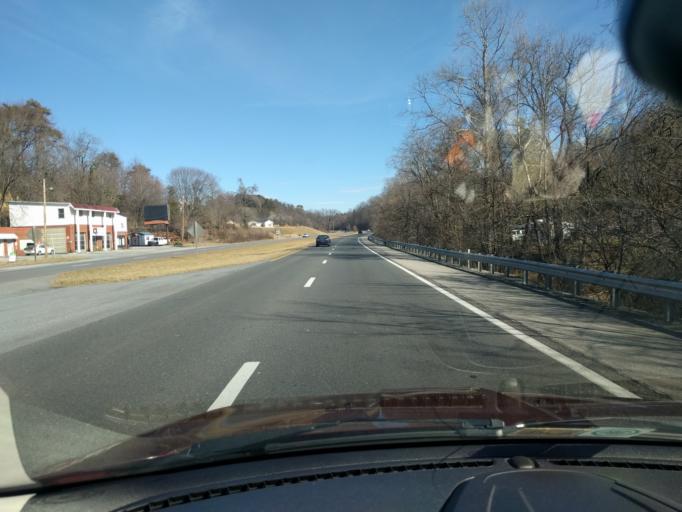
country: US
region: Virginia
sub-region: Botetourt County
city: Laymantown
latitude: 37.3368
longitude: -79.8568
